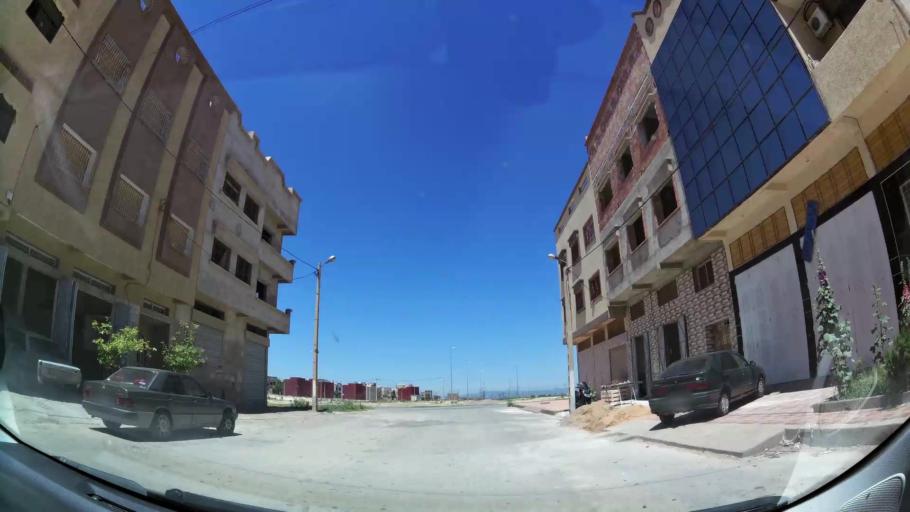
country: MA
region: Oriental
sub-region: Oujda-Angad
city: Oujda
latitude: 34.6792
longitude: -1.8627
